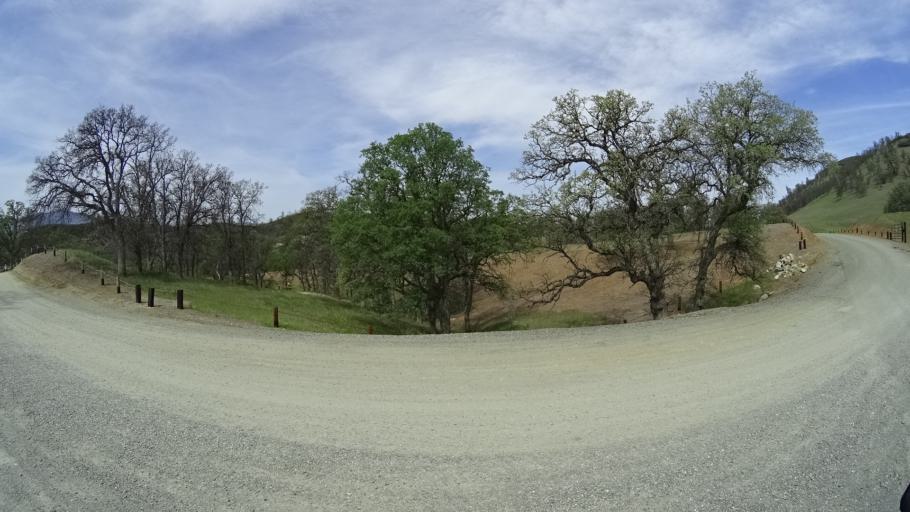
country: US
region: California
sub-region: Glenn County
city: Willows
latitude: 39.5888
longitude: -122.5235
